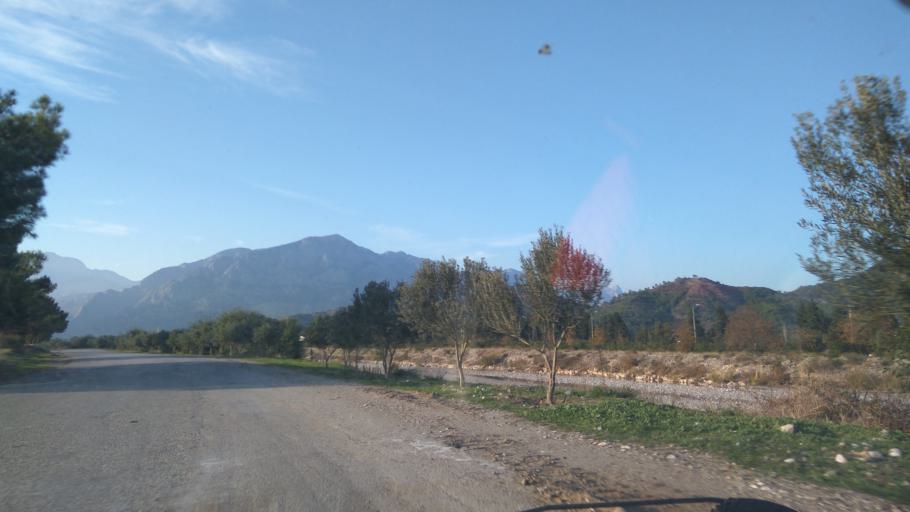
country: TR
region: Antalya
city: Kemer
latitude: 36.5652
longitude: 30.5704
